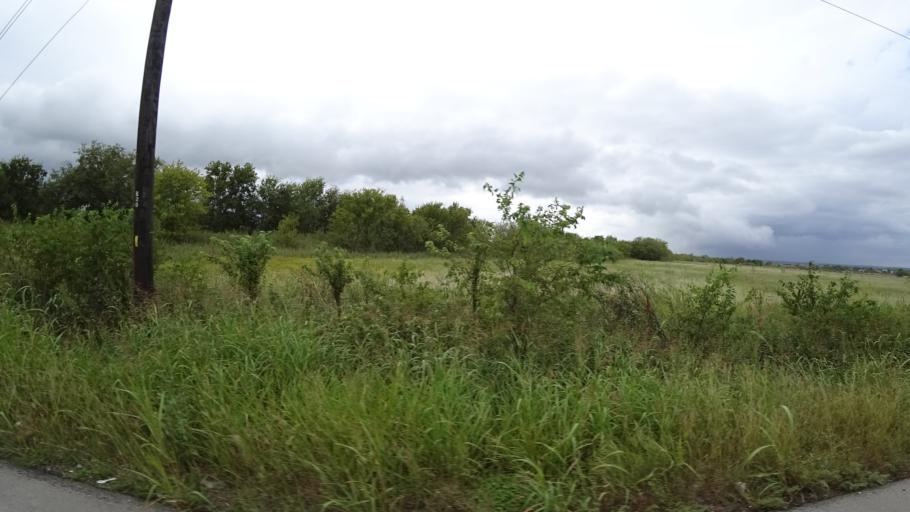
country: US
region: Texas
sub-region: Travis County
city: Onion Creek
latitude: 30.1430
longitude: -97.7295
